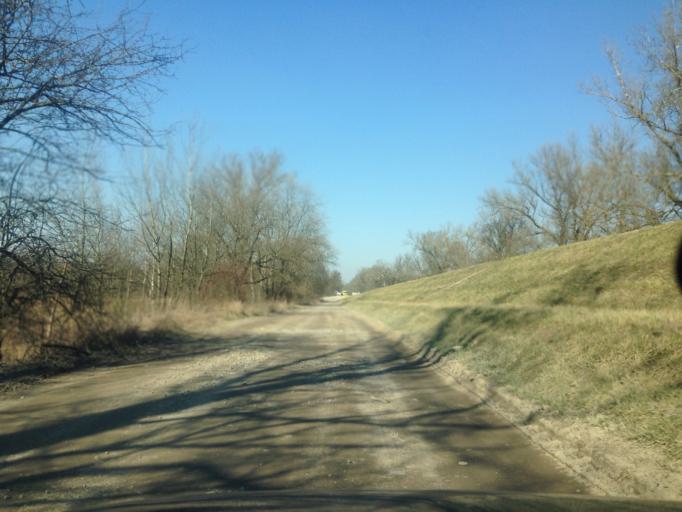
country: PL
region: Masovian Voivodeship
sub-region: Warszawa
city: Wawer
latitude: 52.1451
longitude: 21.1531
